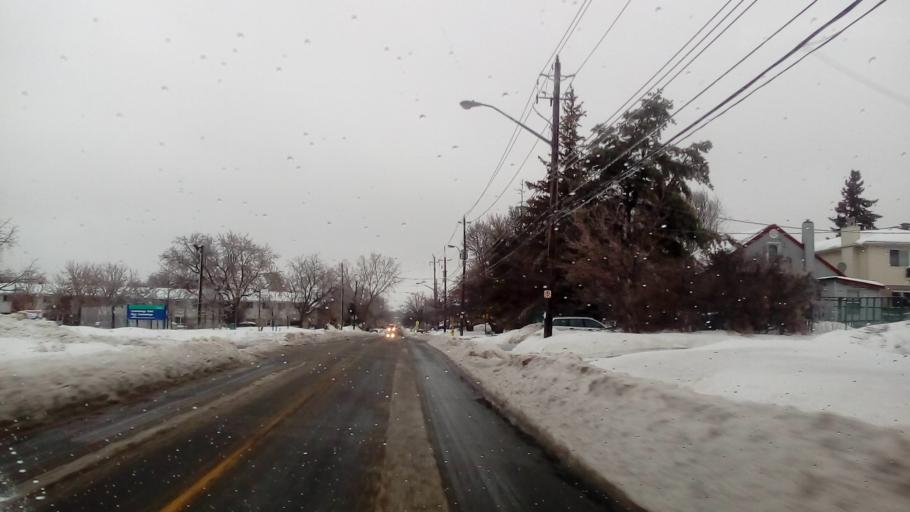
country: CA
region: Ontario
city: Ottawa
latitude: 45.4308
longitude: -75.6342
